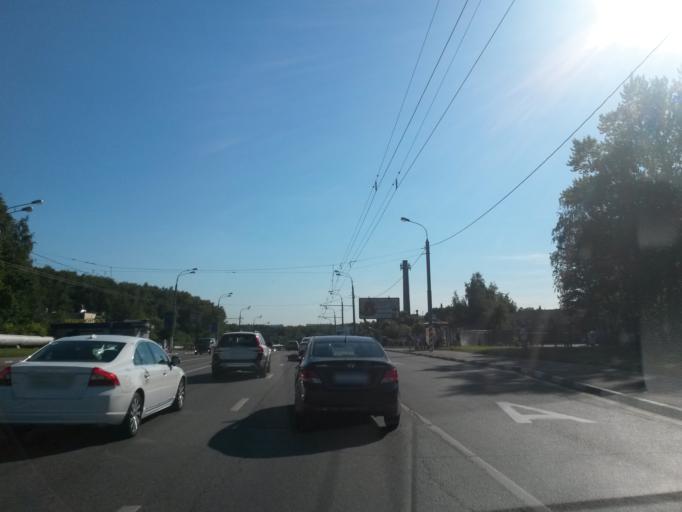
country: RU
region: Moscow
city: Zyuzino
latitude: 55.6485
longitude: 37.5631
